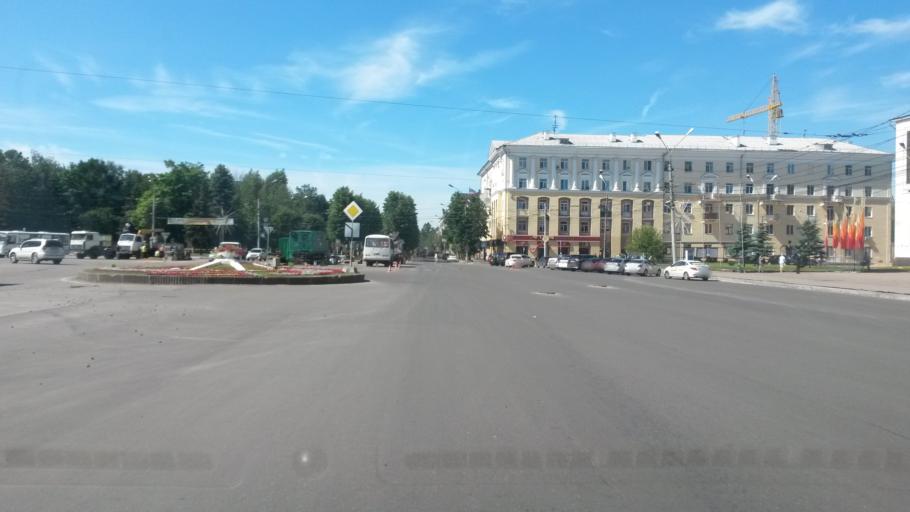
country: RU
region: Jaroslavl
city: Yaroslavl
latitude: 57.6341
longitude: 39.8602
